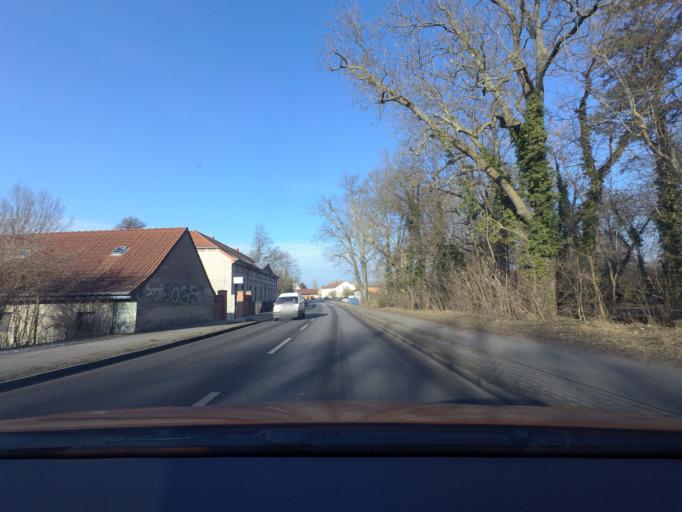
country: DE
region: Berlin
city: Blankenfelde
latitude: 52.6345
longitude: 13.3800
